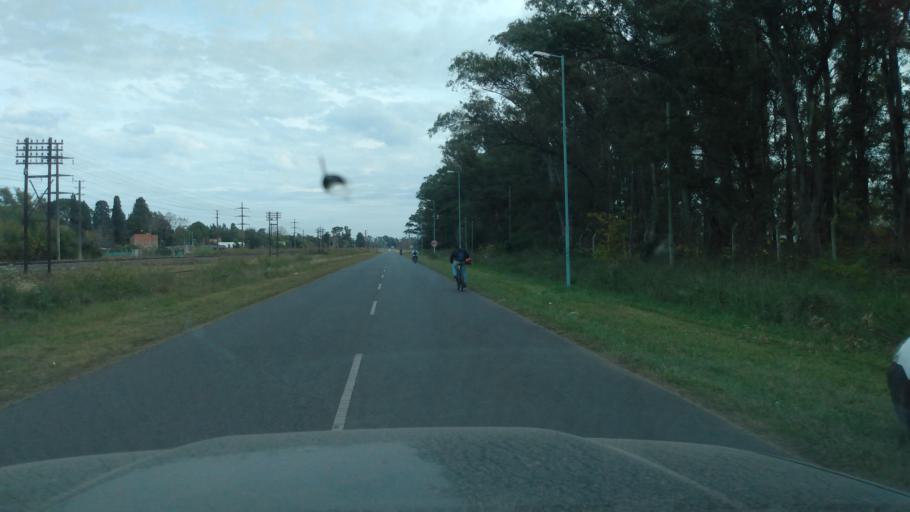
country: AR
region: Buenos Aires
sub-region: Partido de Lujan
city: Lujan
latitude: -34.5866
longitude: -59.1322
